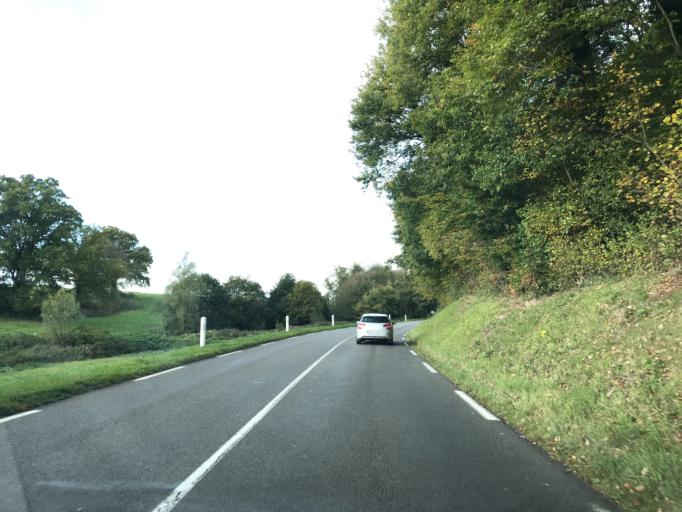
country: FR
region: Haute-Normandie
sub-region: Departement de l'Eure
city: Les Andelys
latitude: 49.2713
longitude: 1.4139
